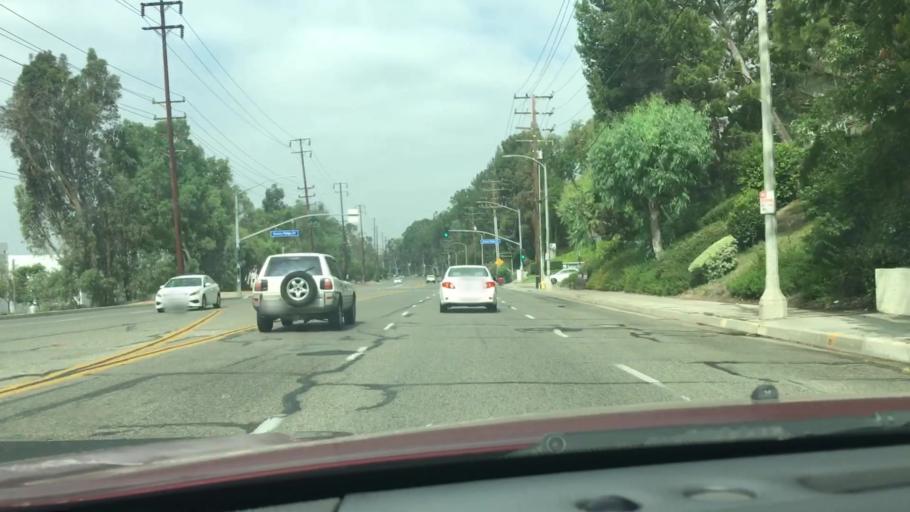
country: US
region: California
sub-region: Orange County
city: Buena Park
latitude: 33.8781
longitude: -117.9682
